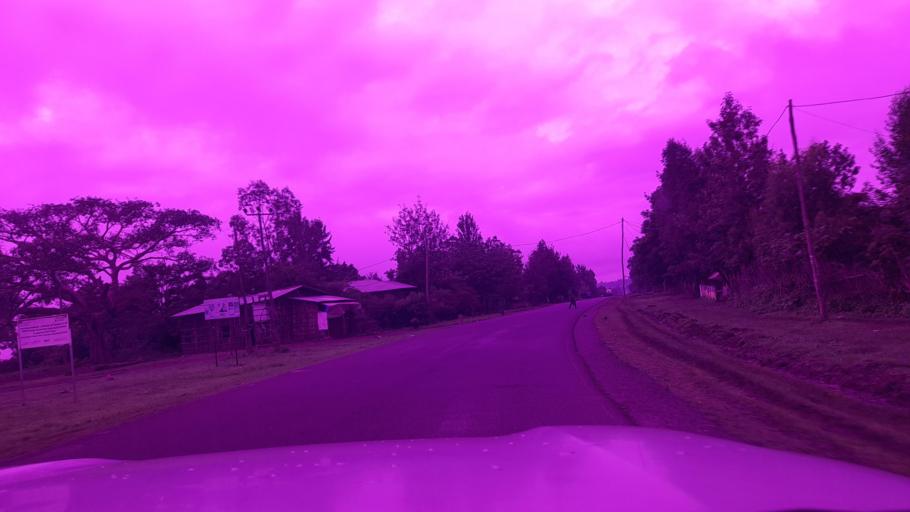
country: ET
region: Oromiya
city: Waliso
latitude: 8.2810
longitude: 37.6870
